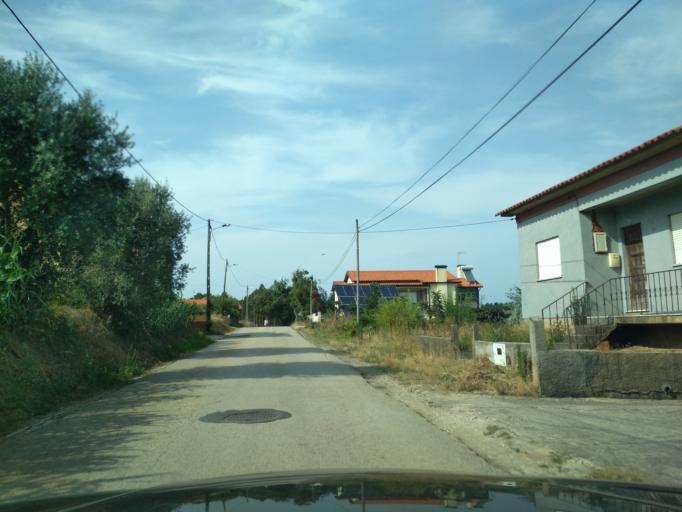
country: PT
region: Aveiro
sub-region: Mealhada
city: Mealhada
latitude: 40.3637
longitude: -8.5071
